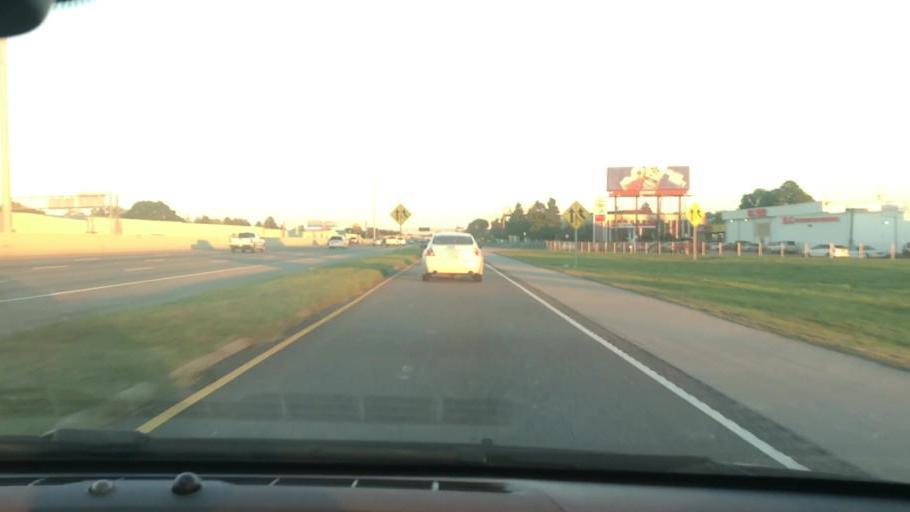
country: US
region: Louisiana
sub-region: Jefferson Parish
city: Metairie Terrace
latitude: 29.9986
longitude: -90.1818
